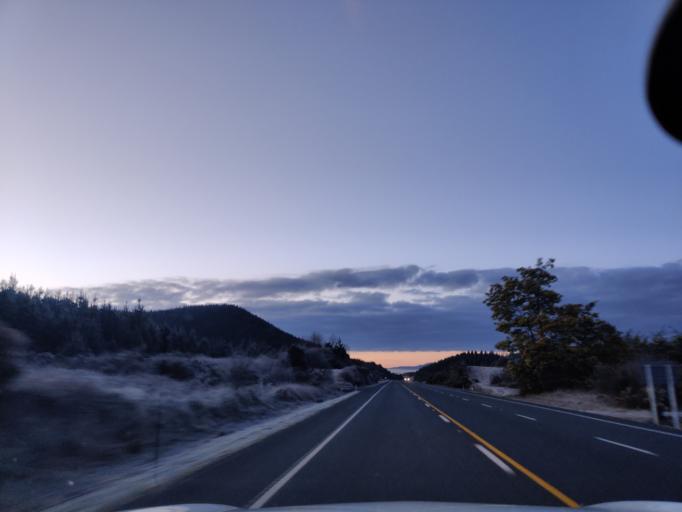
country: NZ
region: Waikato
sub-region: South Waikato District
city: Tokoroa
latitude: -38.3173
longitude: 175.9810
